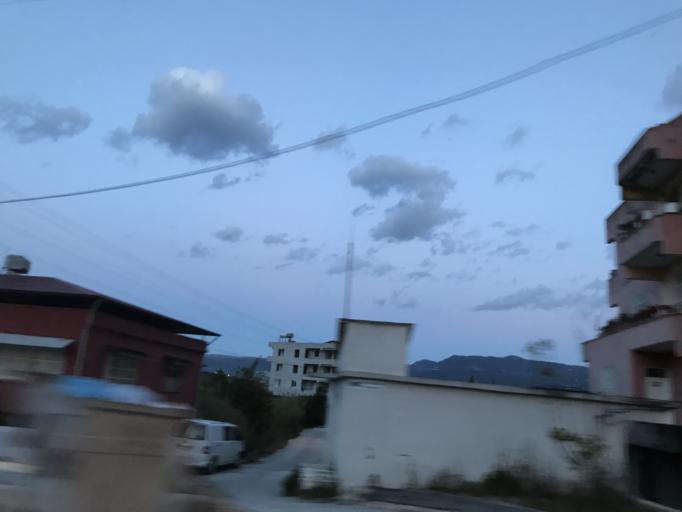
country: TR
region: Hatay
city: Uzunbag
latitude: 36.1341
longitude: 36.0410
